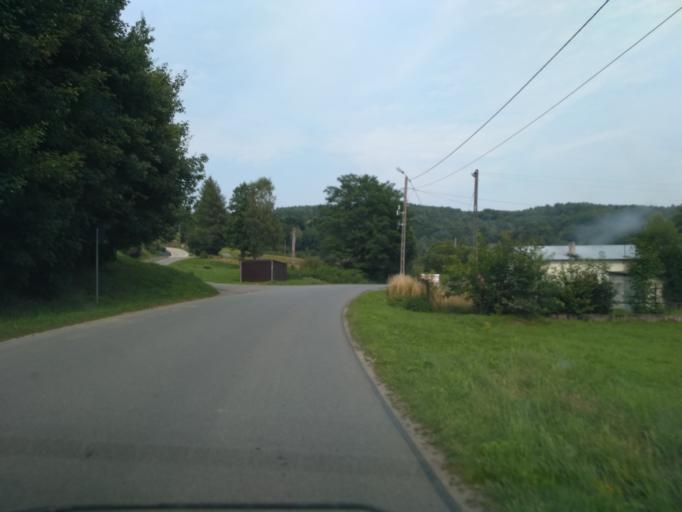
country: PL
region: Subcarpathian Voivodeship
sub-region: Powiat strzyzowski
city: Gwoznica Gorna
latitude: 49.8412
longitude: 21.9758
